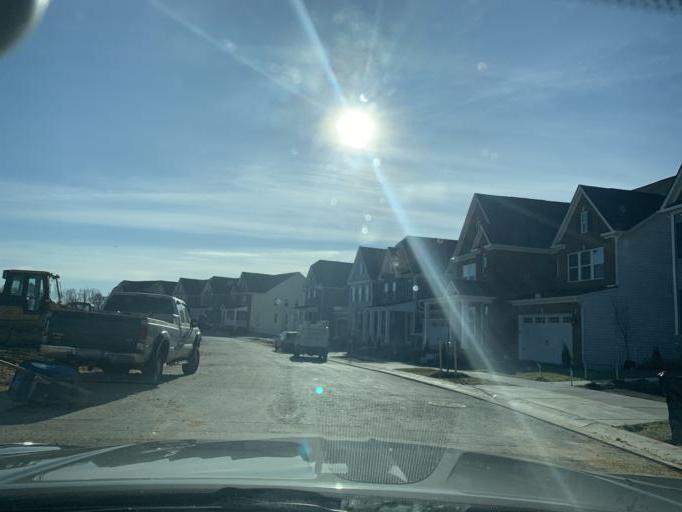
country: US
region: Maryland
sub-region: Anne Arundel County
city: Crofton
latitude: 39.0221
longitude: -76.7282
